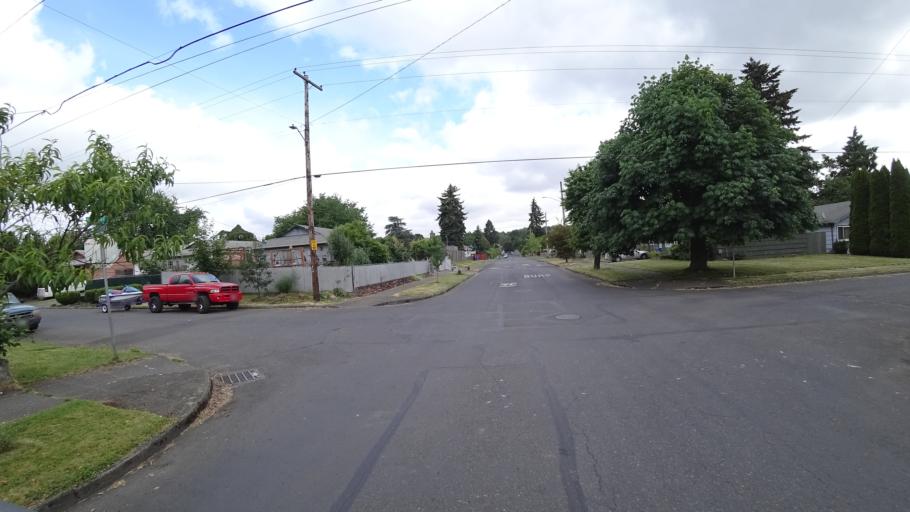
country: US
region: Oregon
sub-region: Multnomah County
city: Lents
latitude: 45.4804
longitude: -122.5598
